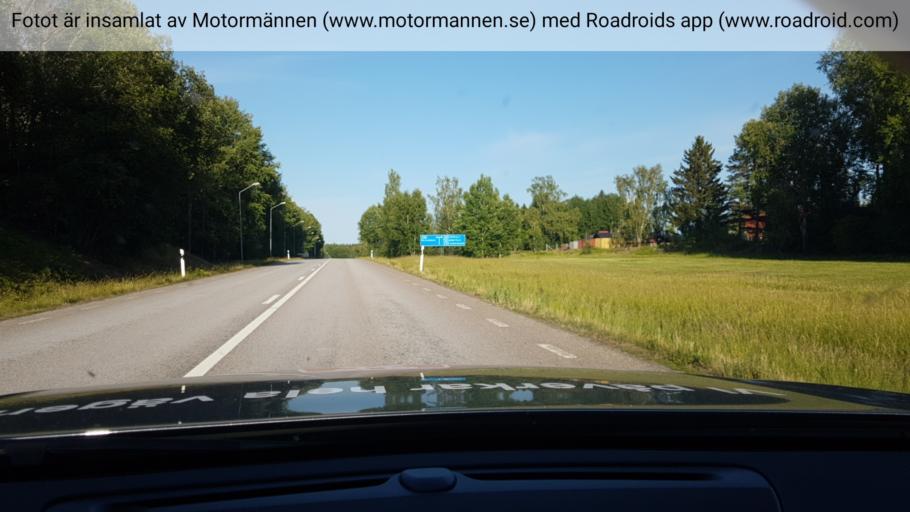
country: SE
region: Uppsala
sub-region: Osthammars Kommun
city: Gimo
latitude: 60.1651
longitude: 18.1842
